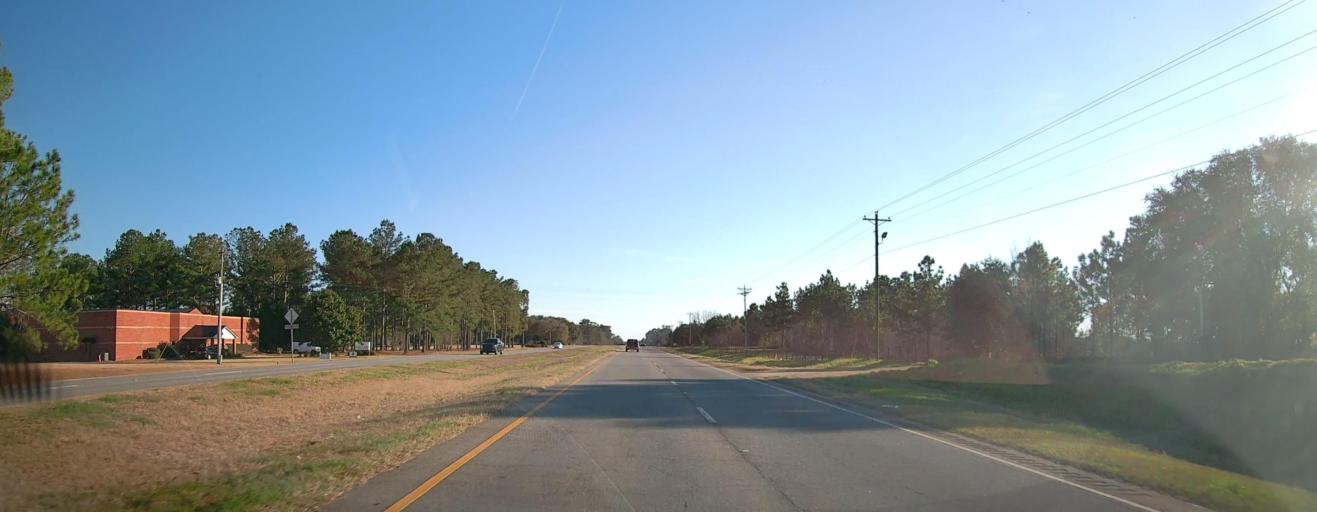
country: US
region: Georgia
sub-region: Lee County
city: Leesburg
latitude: 31.7140
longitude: -84.1725
